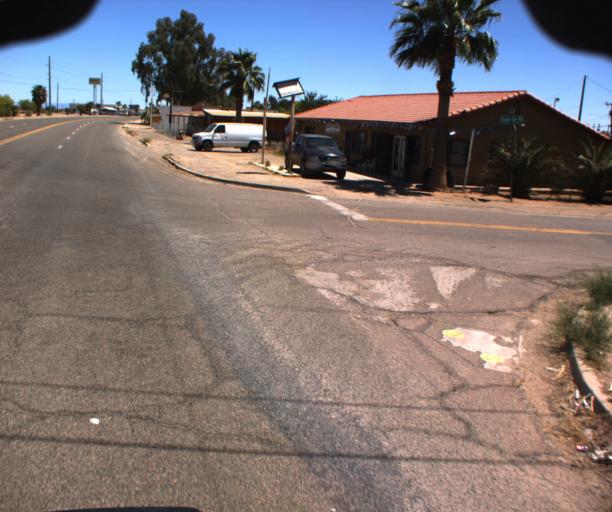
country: US
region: Arizona
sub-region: Yavapai County
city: Congress
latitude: 33.9426
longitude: -113.1767
